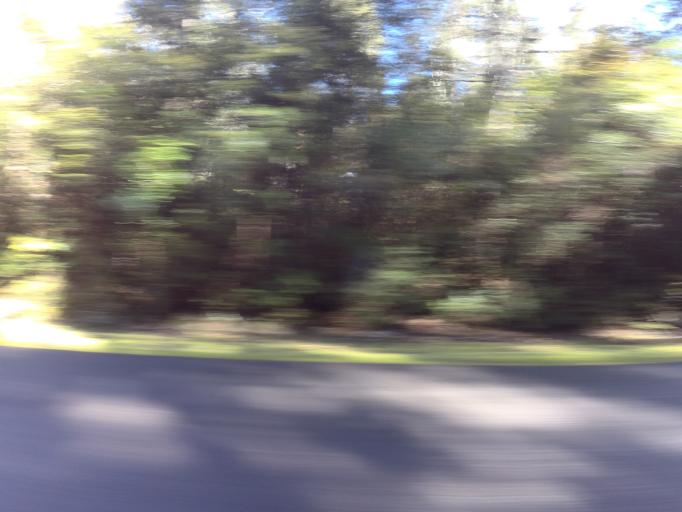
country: AU
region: Tasmania
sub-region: Derwent Valley
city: New Norfolk
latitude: -42.7266
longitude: 146.4325
